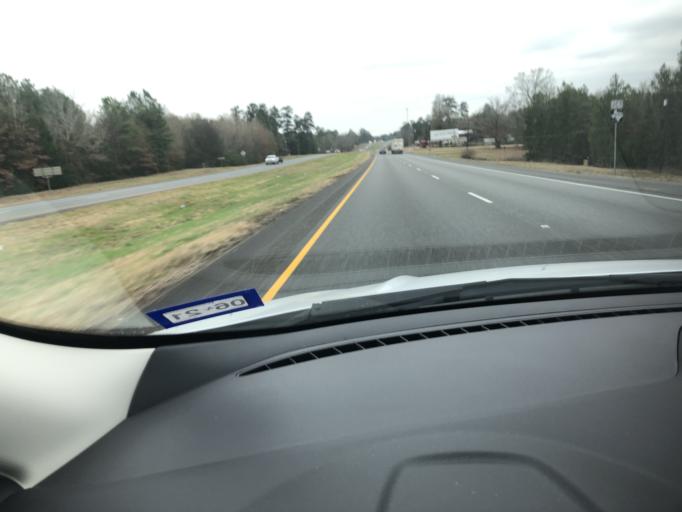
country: US
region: Texas
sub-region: Angelina County
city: Redland
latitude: 31.4421
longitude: -94.7266
